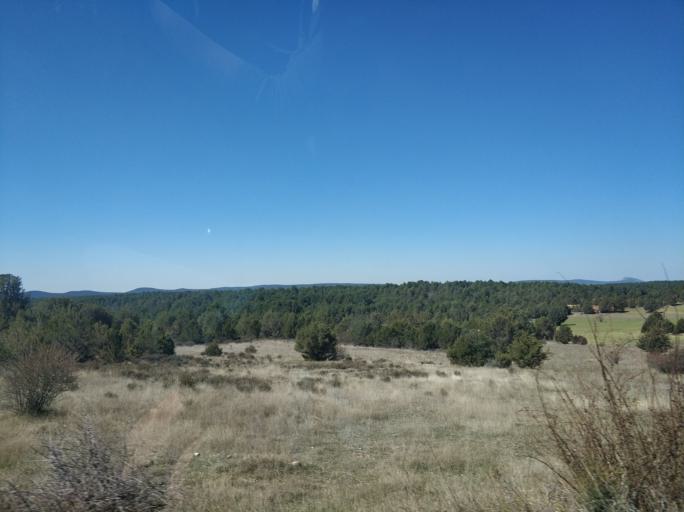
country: ES
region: Castille and Leon
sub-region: Provincia de Soria
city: Herrera de Soria
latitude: 41.7770
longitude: -3.0266
